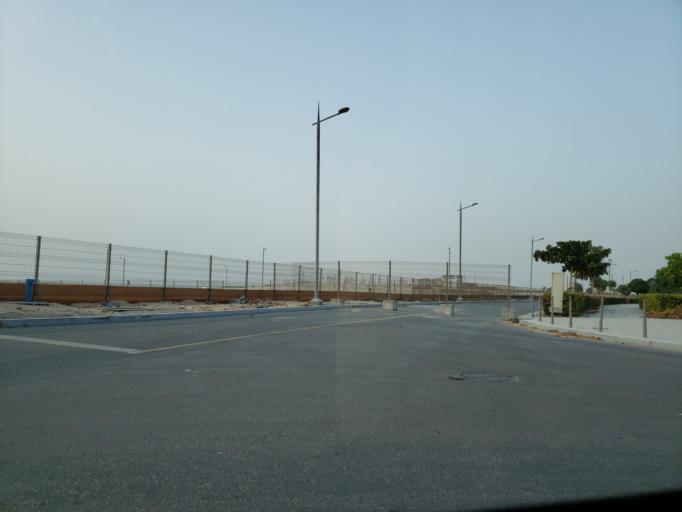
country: AE
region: Ajman
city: Ajman
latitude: 25.4313
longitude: 55.4597
